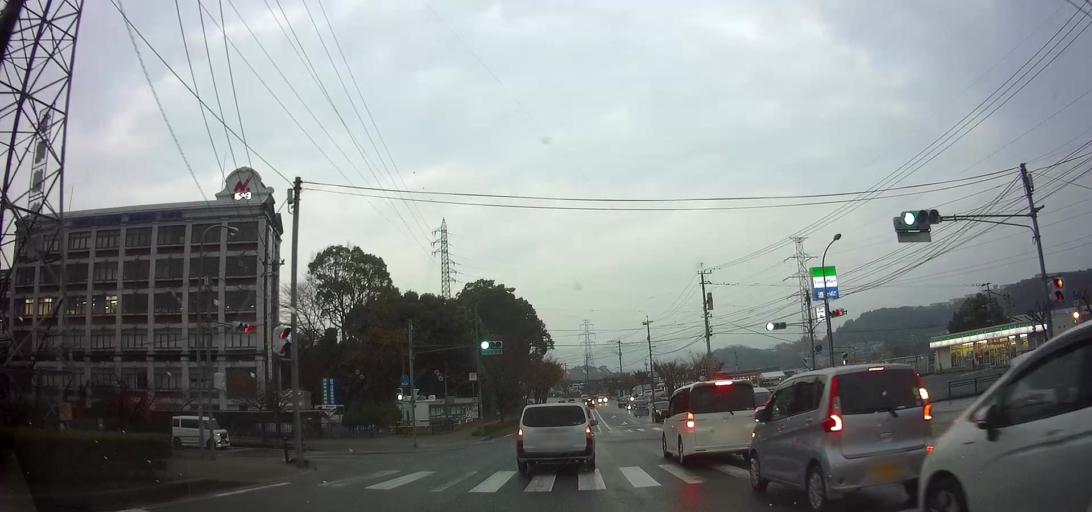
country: JP
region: Nagasaki
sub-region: Isahaya-shi
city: Isahaya
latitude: 32.8399
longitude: 130.0134
